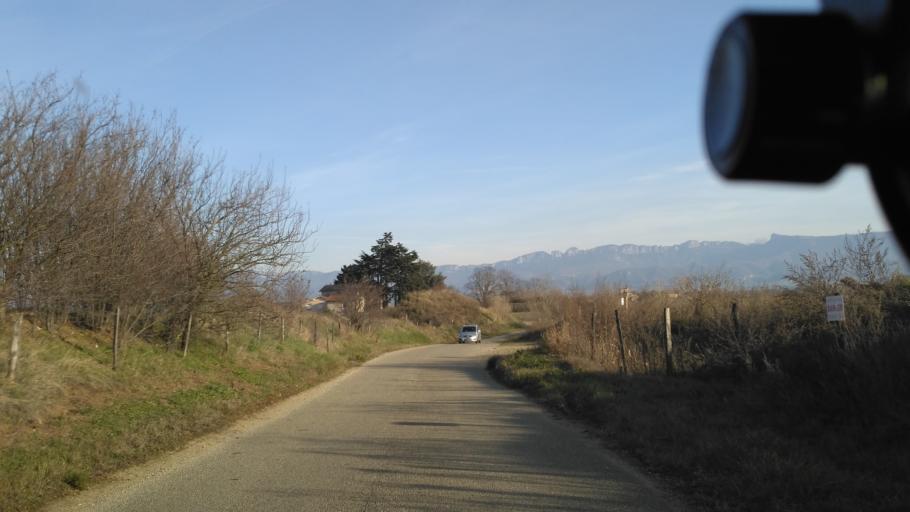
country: FR
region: Rhone-Alpes
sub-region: Departement de la Drome
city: Alixan
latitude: 44.9781
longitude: 5.0146
